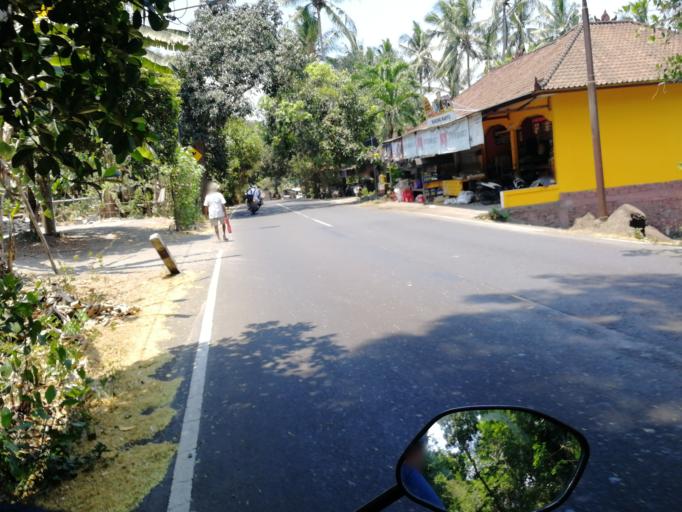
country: ID
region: Bali
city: Padangbai
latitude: -8.5166
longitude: 115.4973
